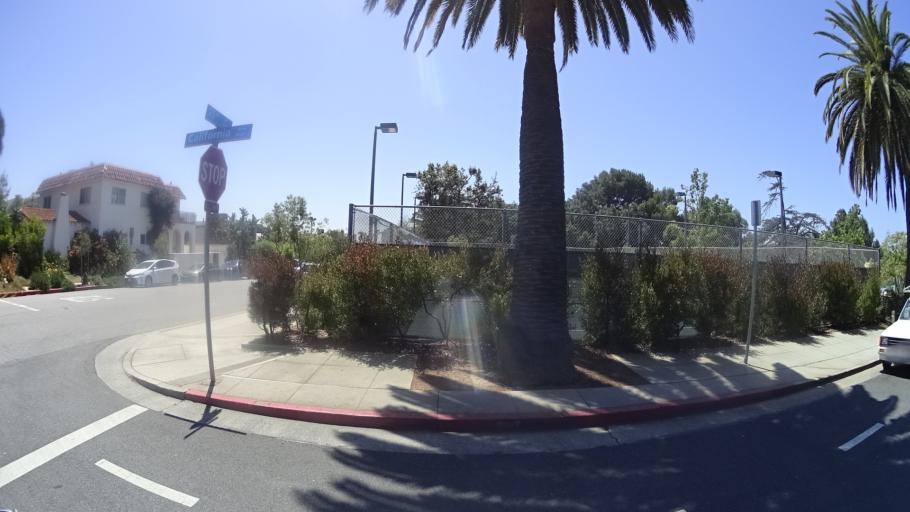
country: US
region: California
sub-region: Los Angeles County
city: Santa Monica
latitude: 34.0367
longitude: -118.4800
